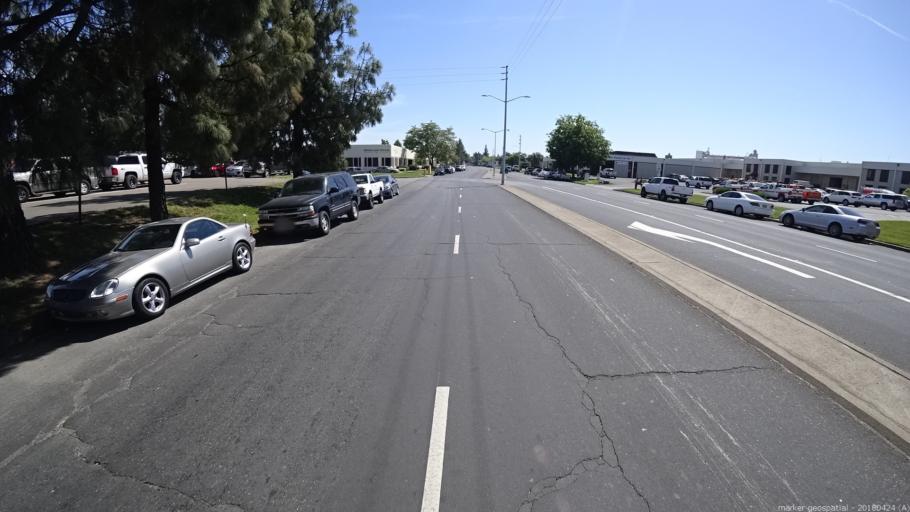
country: US
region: California
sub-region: Yolo County
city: West Sacramento
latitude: 38.5699
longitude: -121.5468
